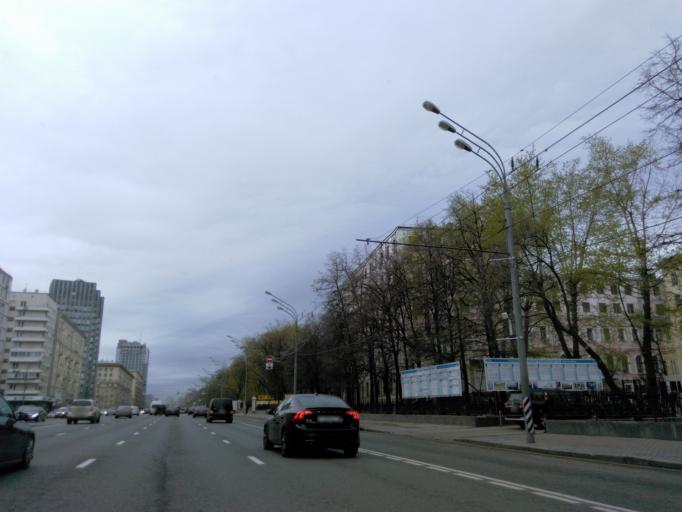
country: RU
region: Moscow
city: Zamoskvorech'ye
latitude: 55.7268
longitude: 37.6082
